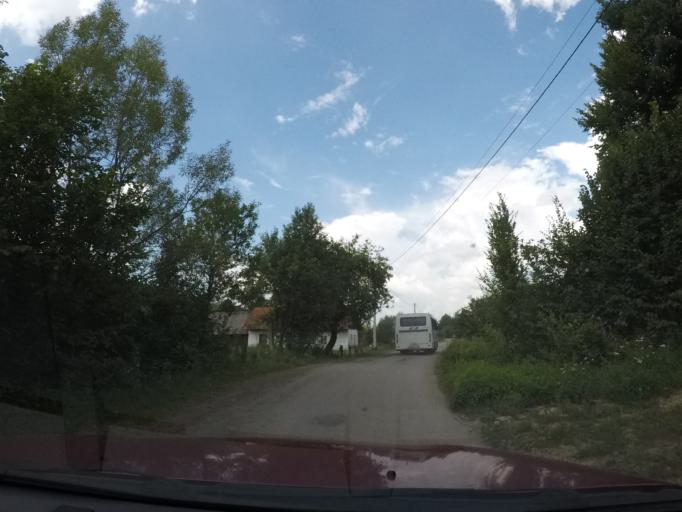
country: UA
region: Zakarpattia
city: Velykyi Bereznyi
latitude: 49.0221
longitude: 22.6130
